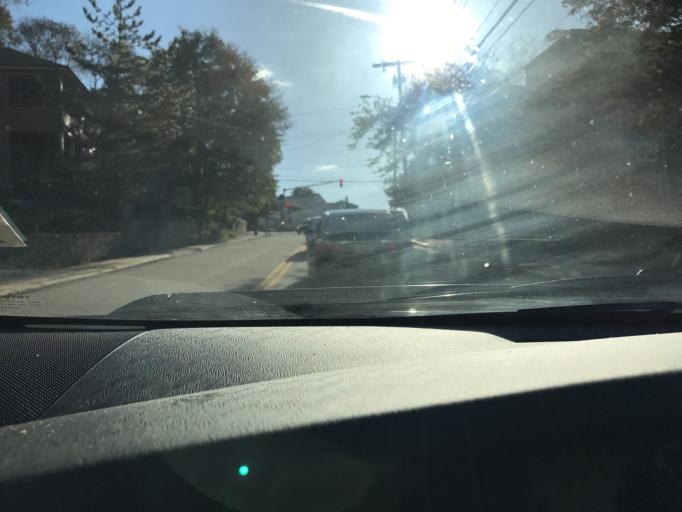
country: US
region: Massachusetts
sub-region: Suffolk County
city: Jamaica Plain
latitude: 42.2739
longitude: -71.1287
